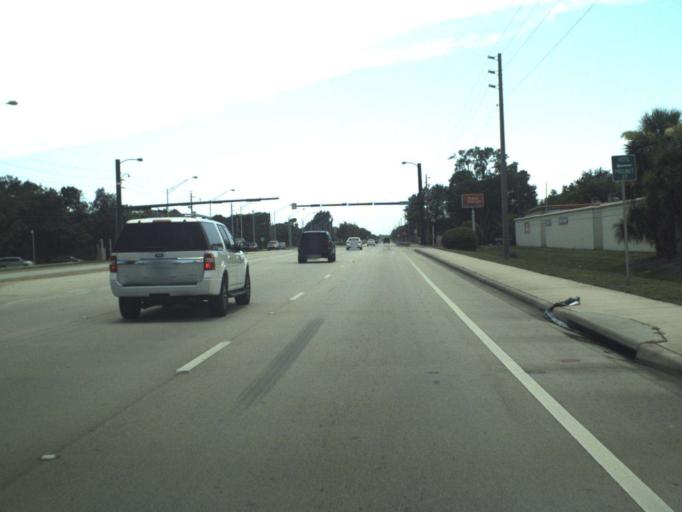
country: US
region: Florida
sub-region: Indian River County
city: Florida Ridge
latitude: 27.5998
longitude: -80.3812
